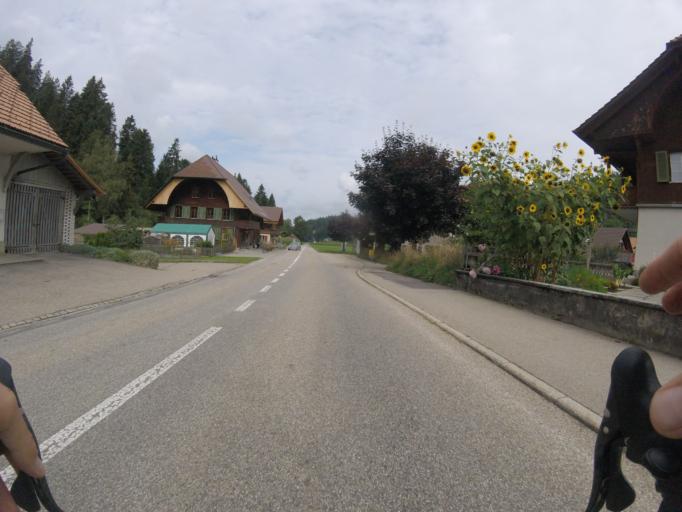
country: CH
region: Bern
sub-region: Emmental District
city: Lutzelfluh
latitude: 46.9872
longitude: 7.6942
